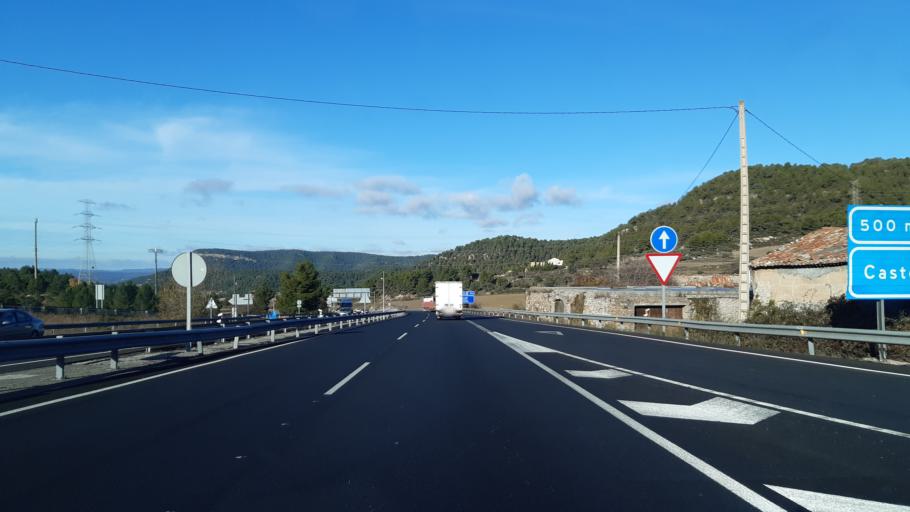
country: ES
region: Catalonia
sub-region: Provincia de Barcelona
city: Castelloli
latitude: 41.5957
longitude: 1.7200
